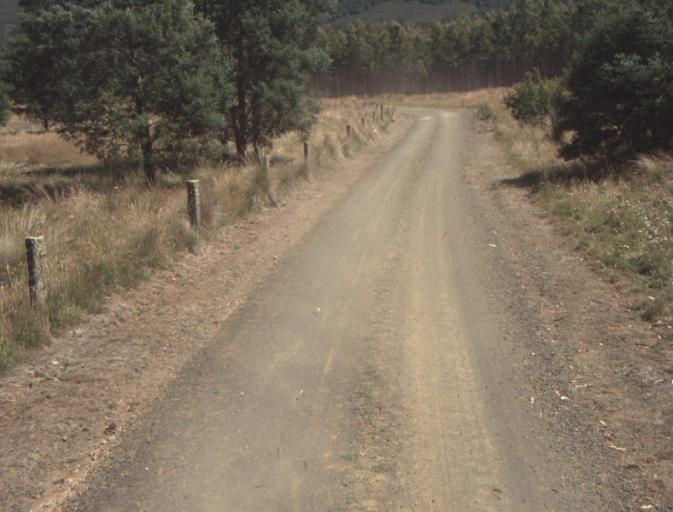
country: AU
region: Tasmania
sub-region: Dorset
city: Scottsdale
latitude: -41.3487
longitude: 147.4527
